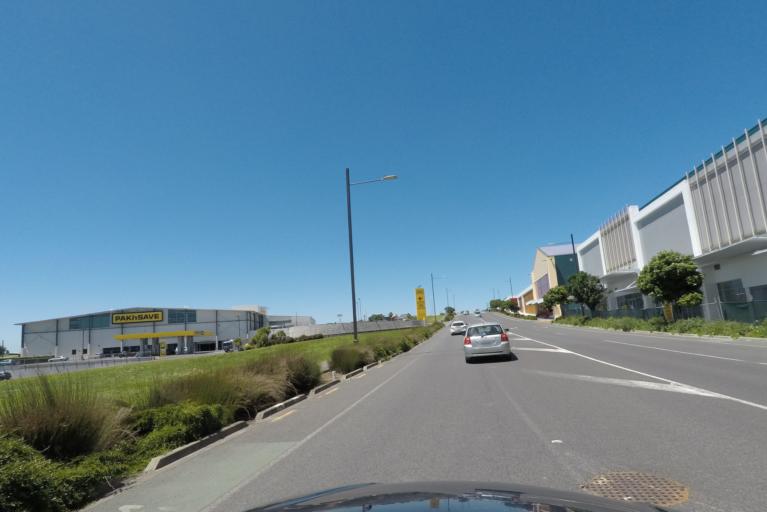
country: NZ
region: Auckland
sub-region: Auckland
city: Rosebank
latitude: -36.8194
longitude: 174.6071
